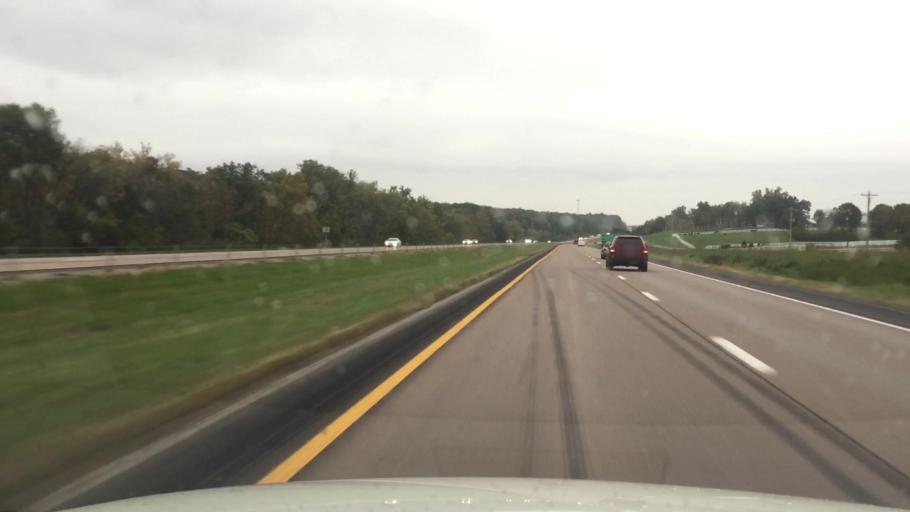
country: US
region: Missouri
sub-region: Boone County
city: Ashland
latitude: 38.8164
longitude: -92.2513
